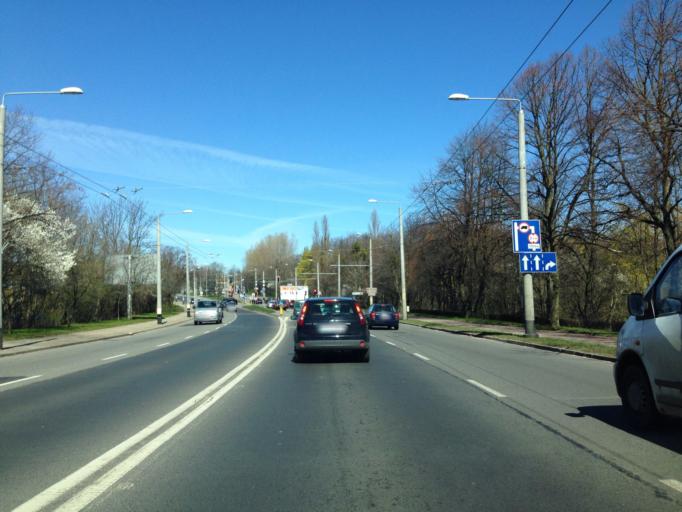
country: PL
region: Pomeranian Voivodeship
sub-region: Sopot
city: Sopot
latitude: 54.4556
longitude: 18.5560
